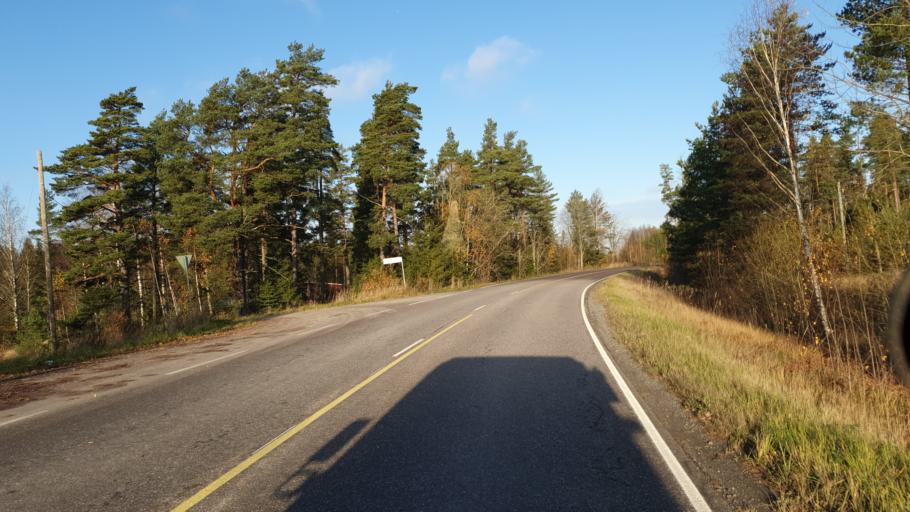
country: FI
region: Uusimaa
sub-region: Helsinki
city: Siuntio
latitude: 60.1978
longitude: 24.1895
